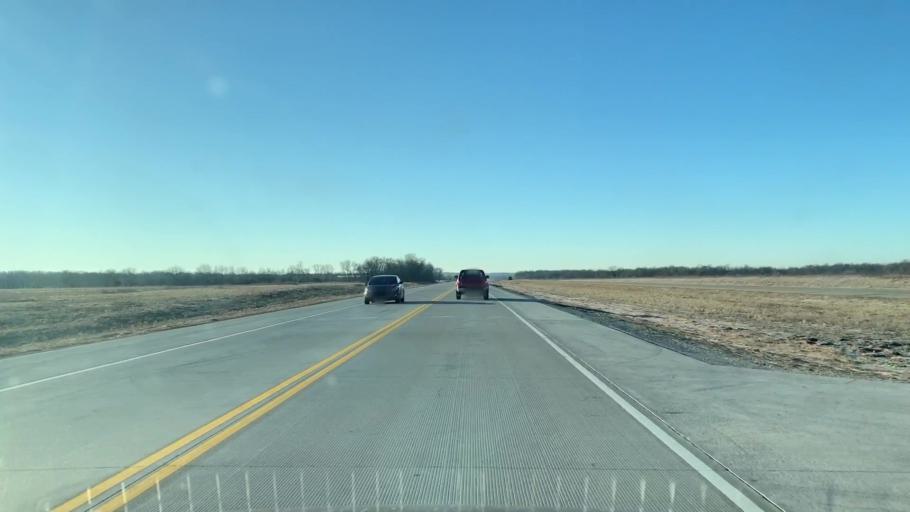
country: US
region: Kansas
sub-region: Bourbon County
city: Fort Scott
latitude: 37.7244
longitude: -94.7043
